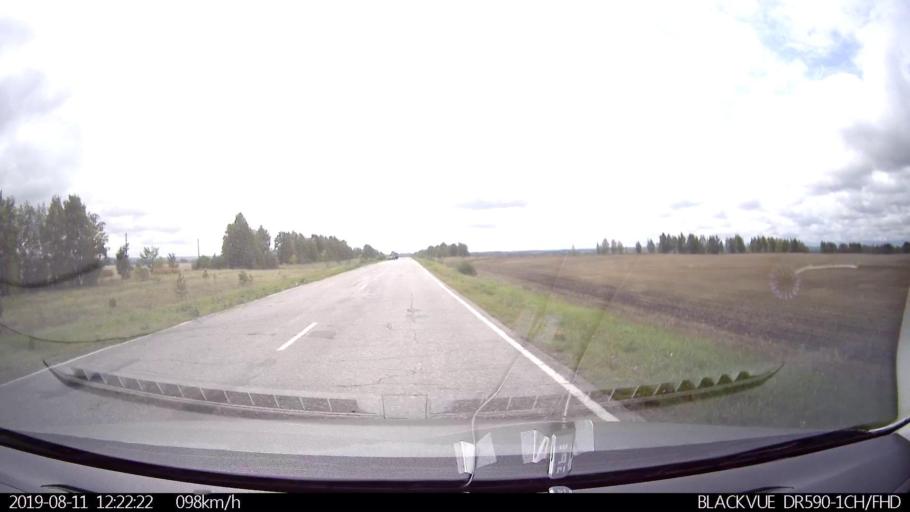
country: RU
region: Ulyanovsk
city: Ignatovka
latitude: 53.9087
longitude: 47.9549
